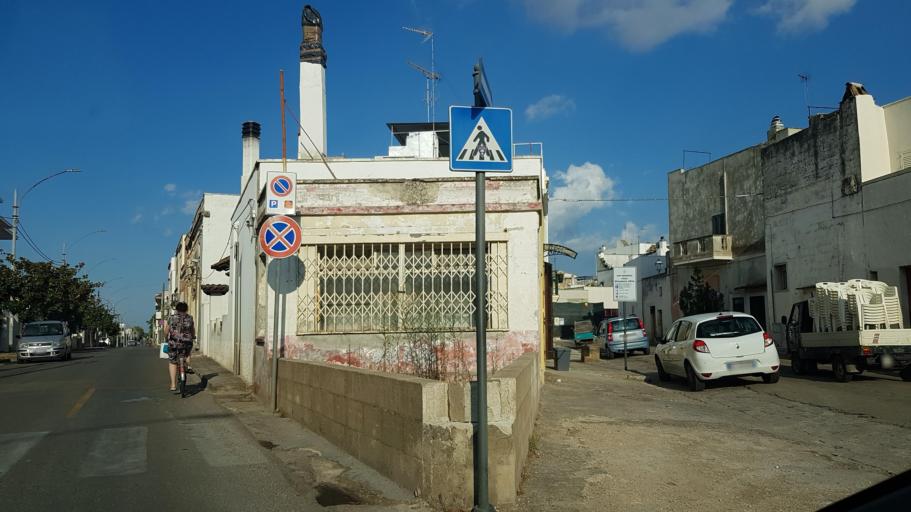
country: IT
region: Apulia
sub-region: Provincia di Lecce
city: Miggiano
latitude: 39.9652
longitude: 18.3082
